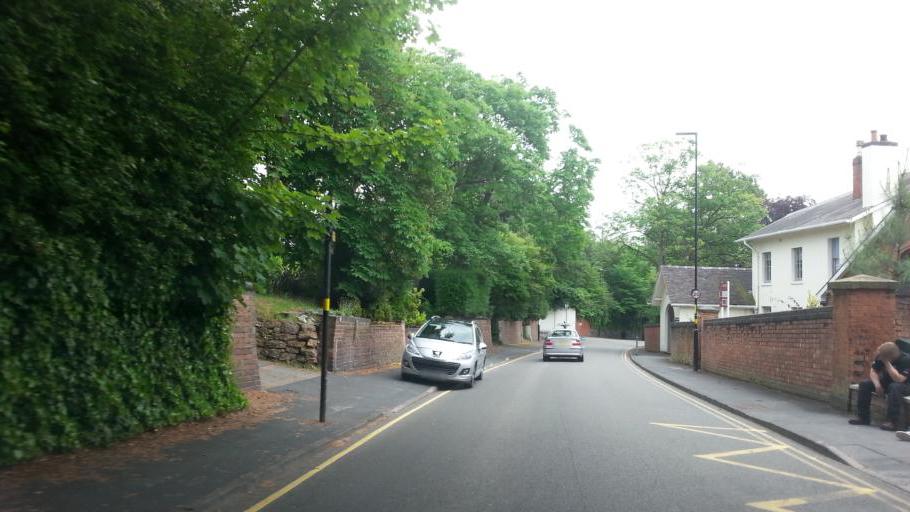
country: GB
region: England
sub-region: City and Borough of Birmingham
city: Birmingham
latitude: 52.4681
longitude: -1.9120
